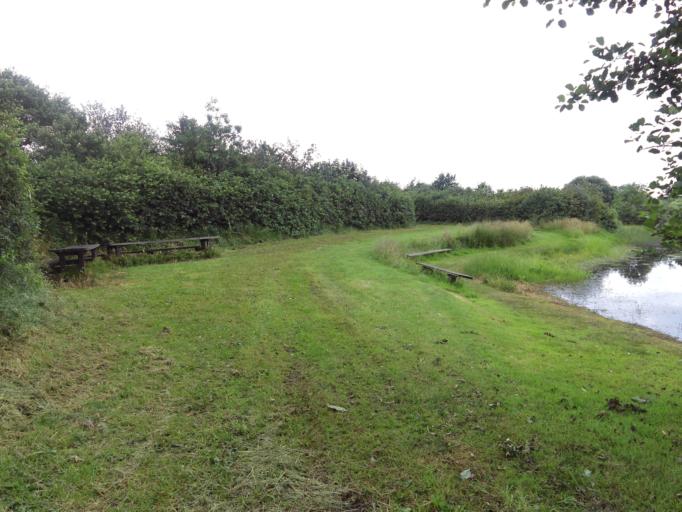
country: DK
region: South Denmark
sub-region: Tonder Kommune
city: Toftlund
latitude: 55.1172
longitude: 9.0775
